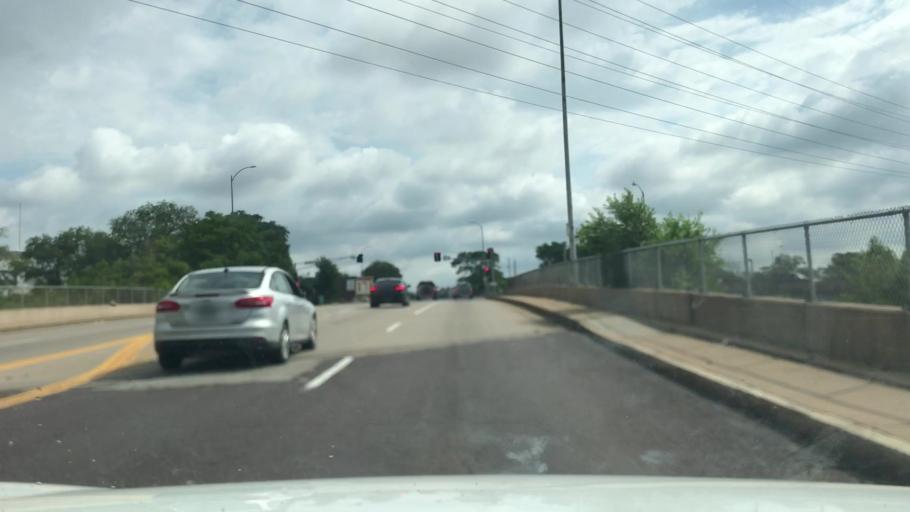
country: US
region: Missouri
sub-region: City of Saint Louis
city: St. Louis
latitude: 38.6214
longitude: -90.2566
